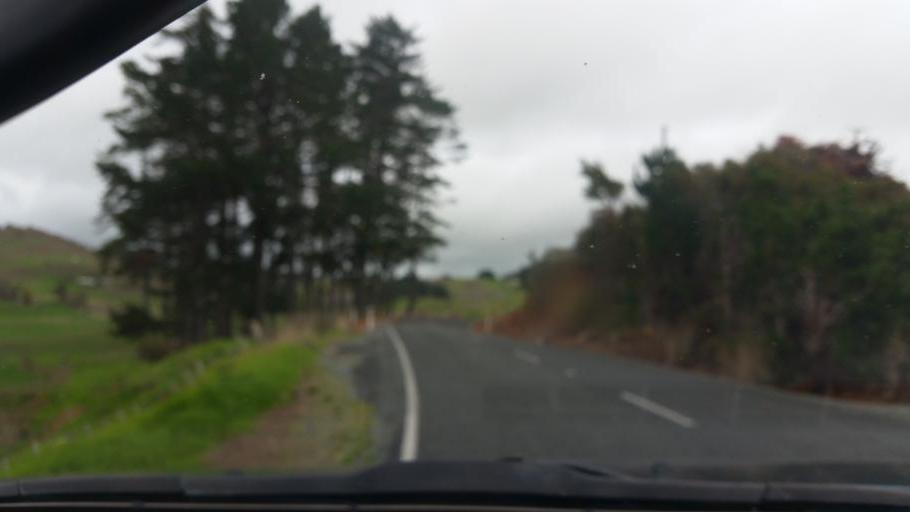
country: NZ
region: Northland
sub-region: Kaipara District
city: Dargaville
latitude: -36.0060
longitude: 173.9669
